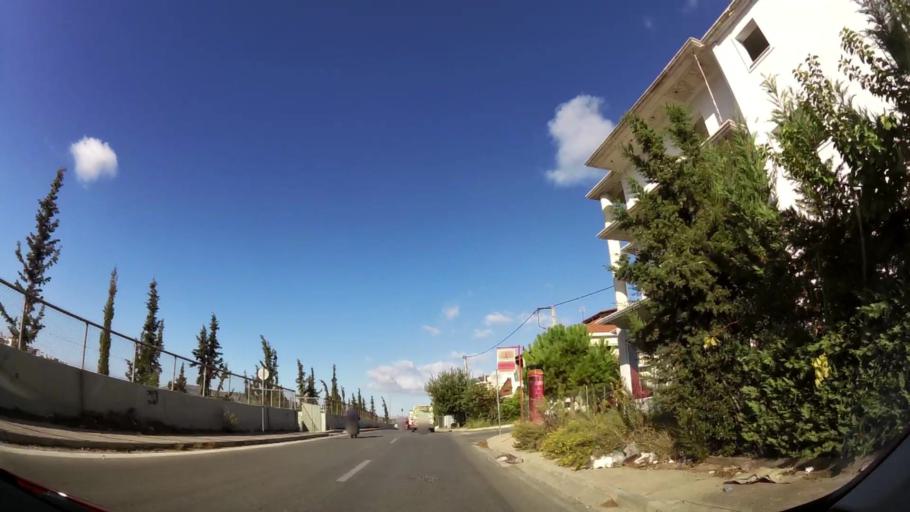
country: GR
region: Attica
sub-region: Nomarchia Anatolikis Attikis
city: Acharnes
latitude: 38.0655
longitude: 23.7401
